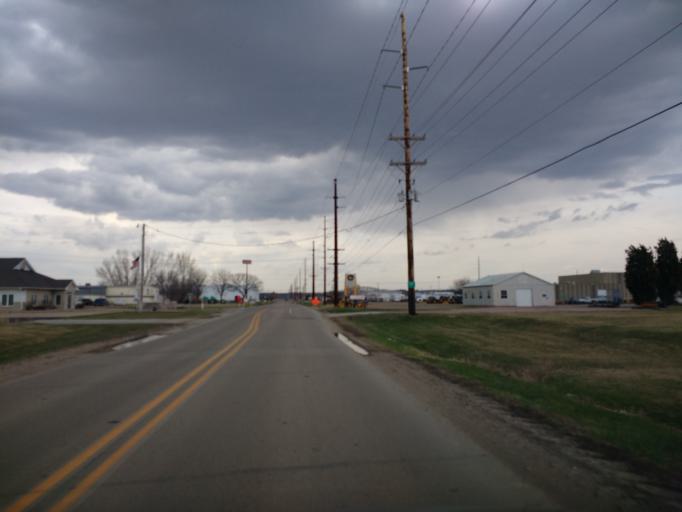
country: US
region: Iowa
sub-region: Woodbury County
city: Sergeant Bluff
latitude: 42.4209
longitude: -96.3698
